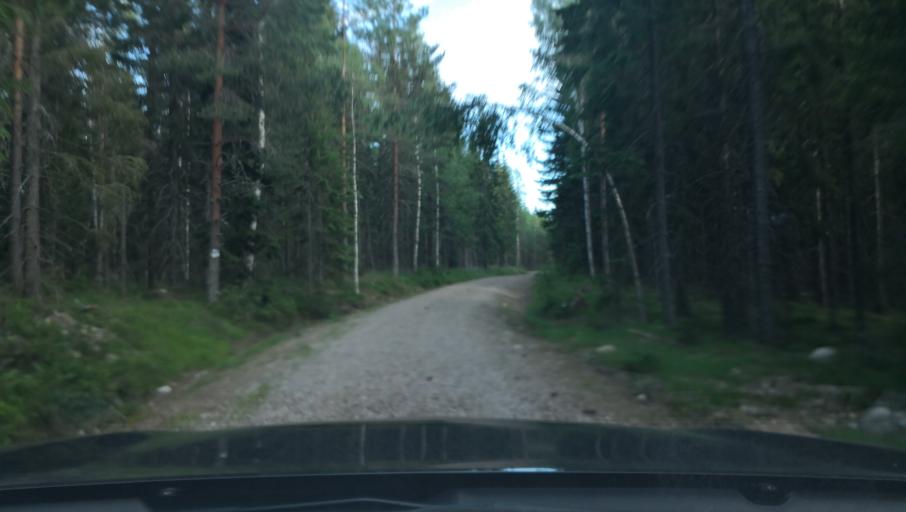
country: SE
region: Dalarna
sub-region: Ludvika Kommun
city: Ludvika
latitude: 60.0752
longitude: 15.2900
